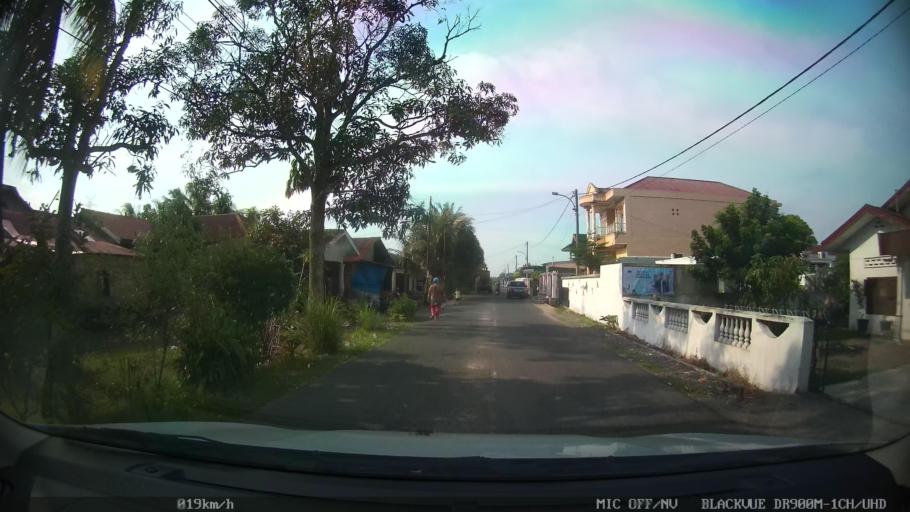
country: ID
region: North Sumatra
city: Binjai
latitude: 3.6094
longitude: 98.5103
